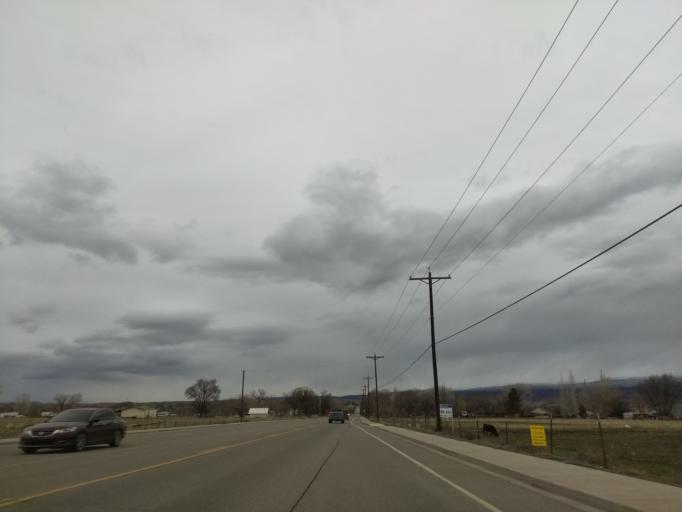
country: US
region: Colorado
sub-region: Mesa County
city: Fruitvale
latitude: 39.0617
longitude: -108.5152
